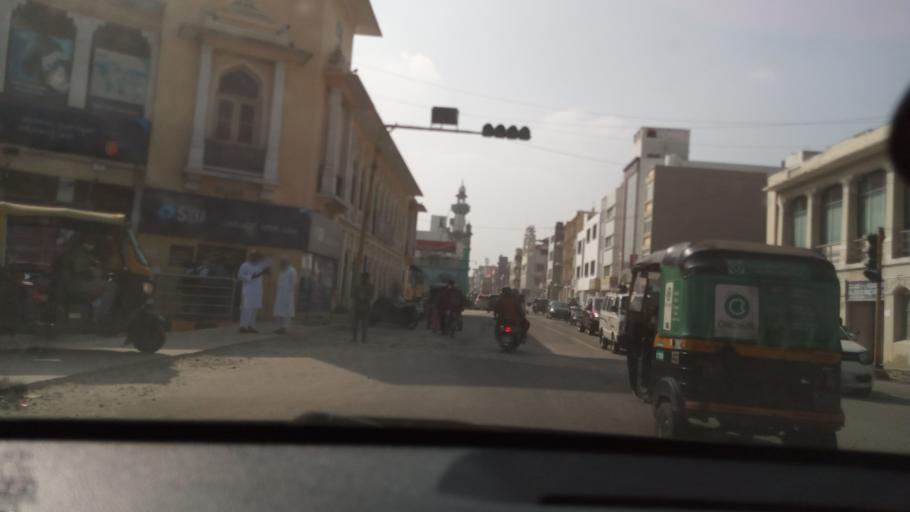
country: IN
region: Karnataka
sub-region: Mysore
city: Mysore
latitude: 12.3141
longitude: 76.6565
